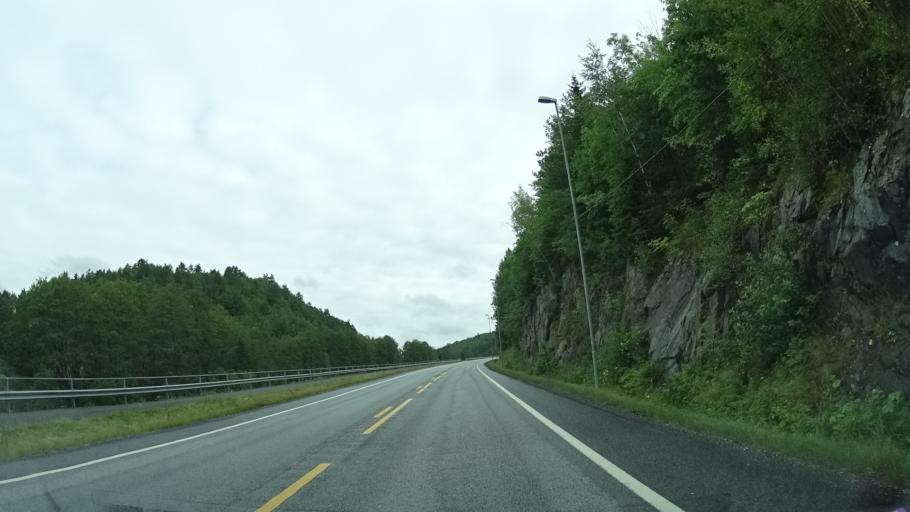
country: NO
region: Aust-Agder
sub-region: Arendal
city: Arendal
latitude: 58.5671
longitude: 8.8250
